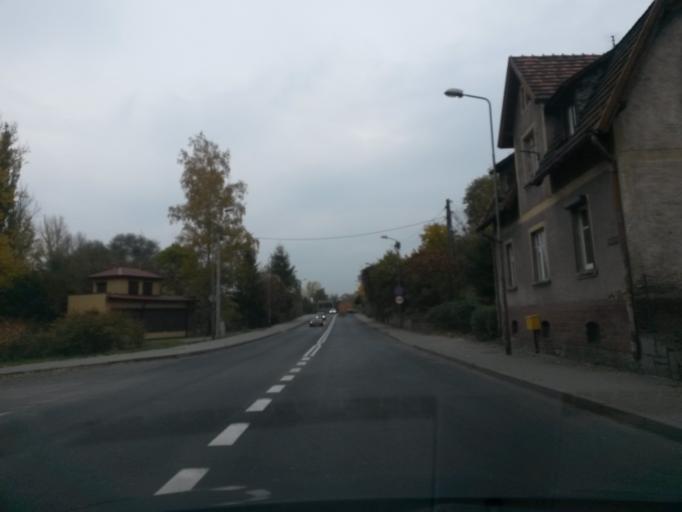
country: PL
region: Lower Silesian Voivodeship
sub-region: Powiat klodzki
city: Klodzko
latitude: 50.4472
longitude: 16.6597
